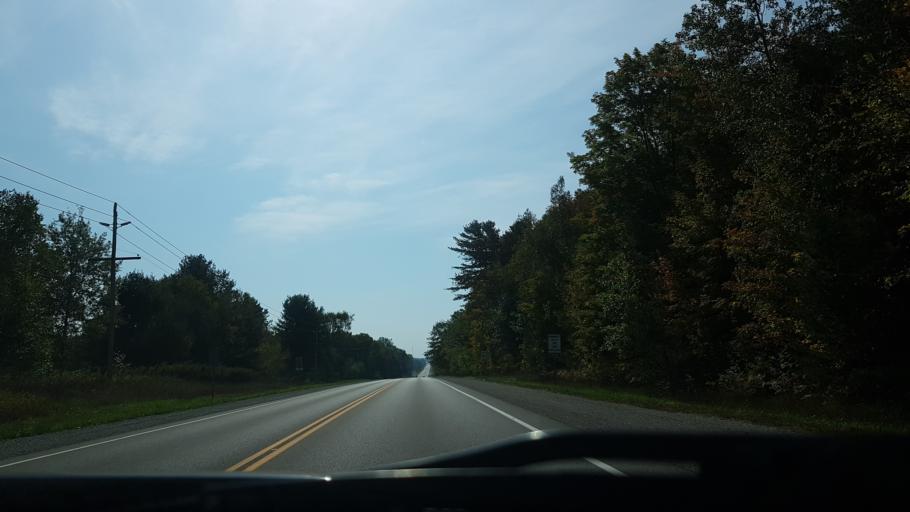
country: CA
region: Ontario
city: Orillia
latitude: 44.7247
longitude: -79.2863
